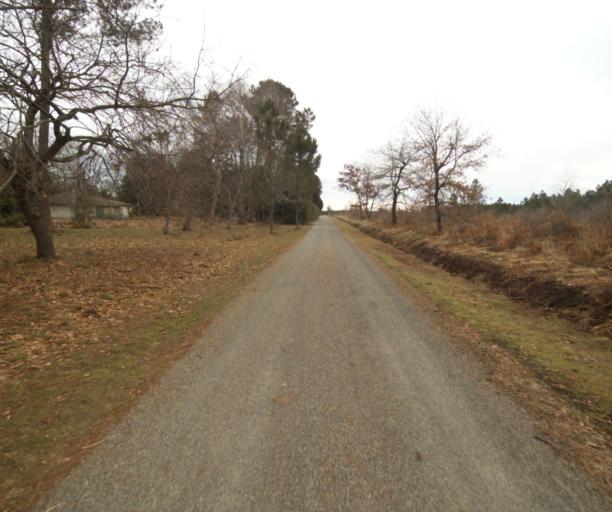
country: FR
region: Aquitaine
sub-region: Departement des Landes
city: Gabarret
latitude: 44.0263
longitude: -0.0313
